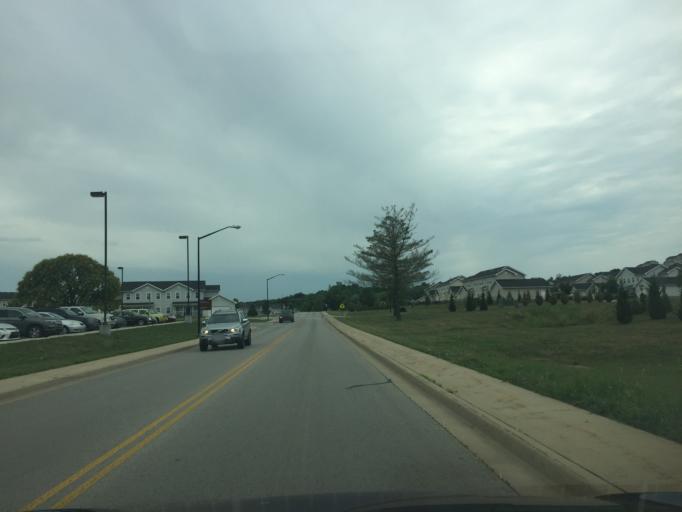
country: US
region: Kansas
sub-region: Leavenworth County
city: Leavenworth
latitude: 39.3442
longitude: -94.9389
